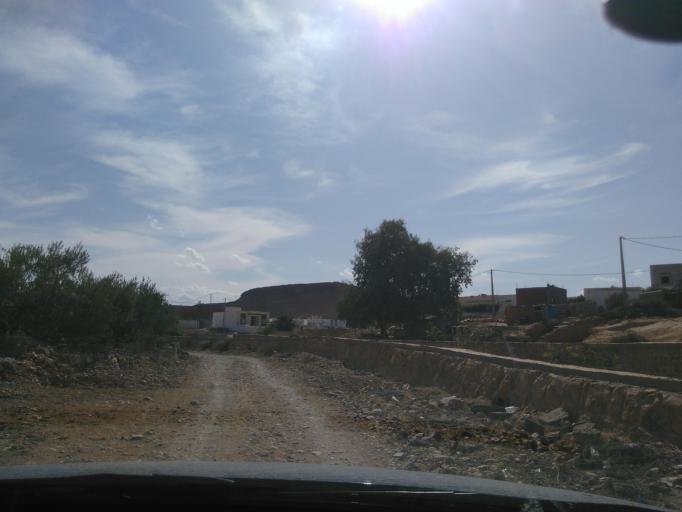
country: TN
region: Tataouine
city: Tataouine
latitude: 32.9156
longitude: 10.4207
